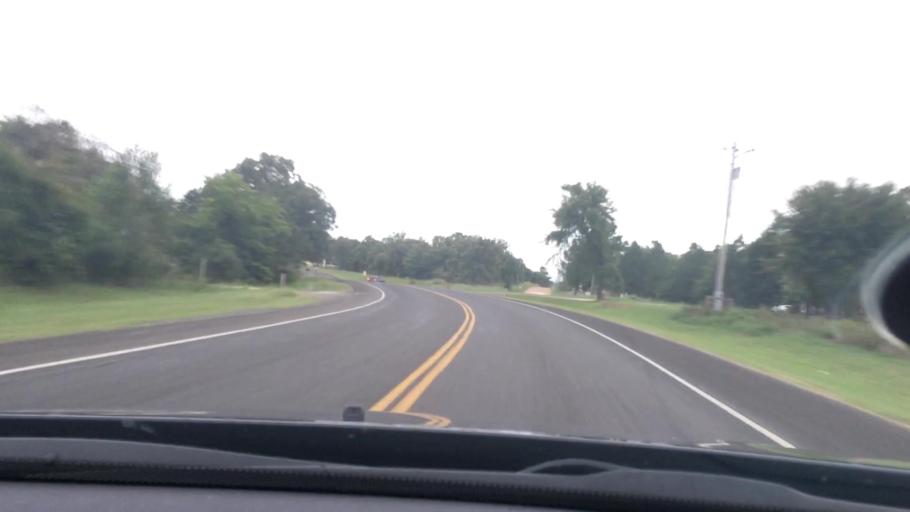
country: US
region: Oklahoma
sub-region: Sequoyah County
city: Vian
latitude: 35.5679
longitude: -94.9853
